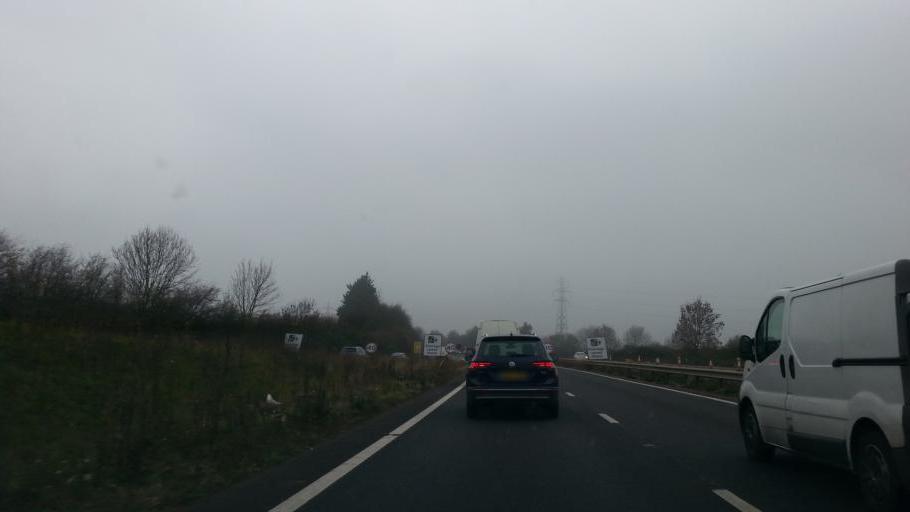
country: GB
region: England
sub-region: Cambridgeshire
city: Waterbeach
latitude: 52.2297
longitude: 0.1783
